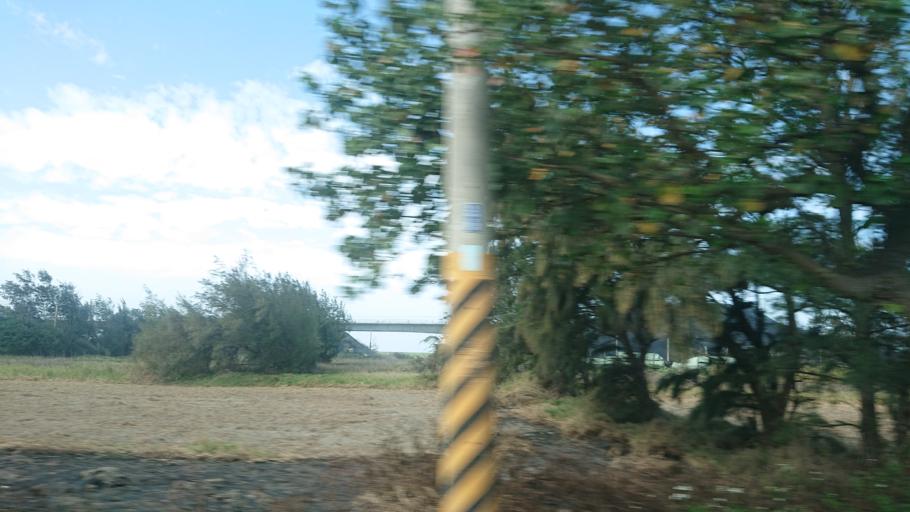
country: TW
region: Taiwan
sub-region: Changhua
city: Chang-hua
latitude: 23.9115
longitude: 120.3105
